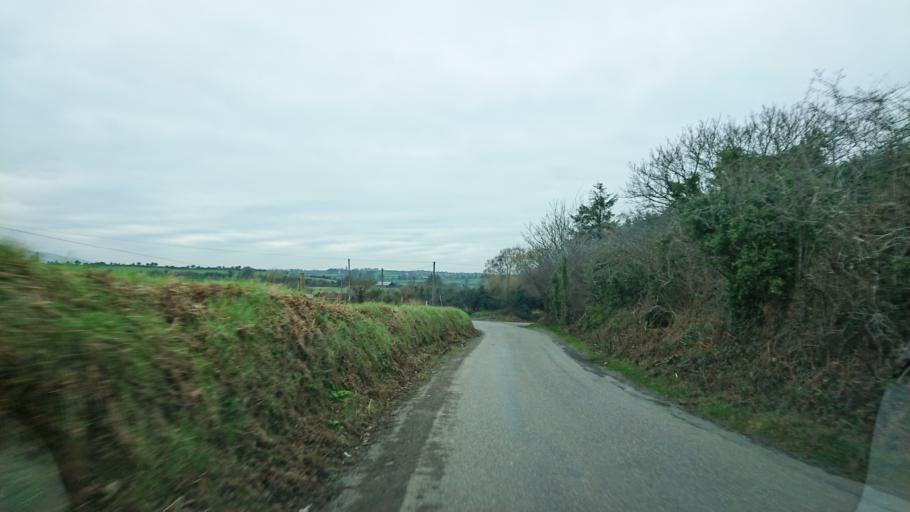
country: IE
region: Munster
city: Carrick-on-Suir
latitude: 52.2751
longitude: -7.4105
